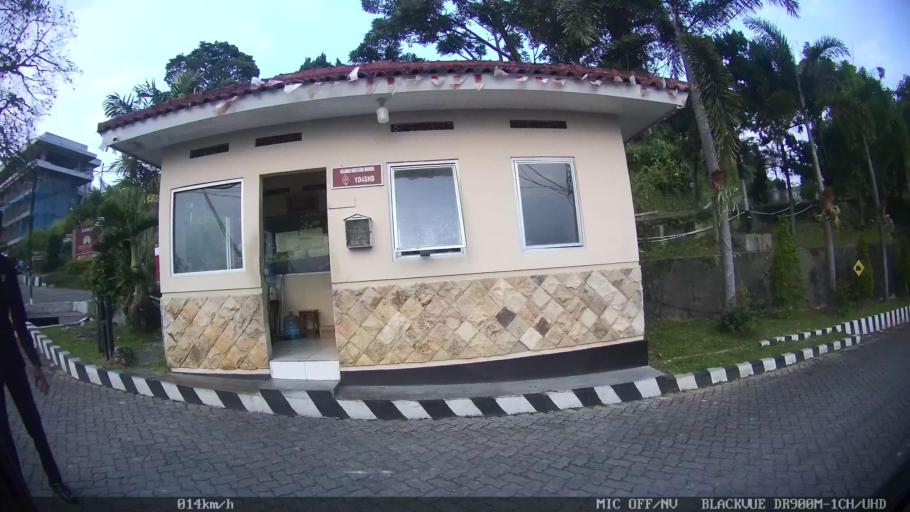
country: ID
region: Lampung
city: Bandarlampung
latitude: -5.4110
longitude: 105.2623
